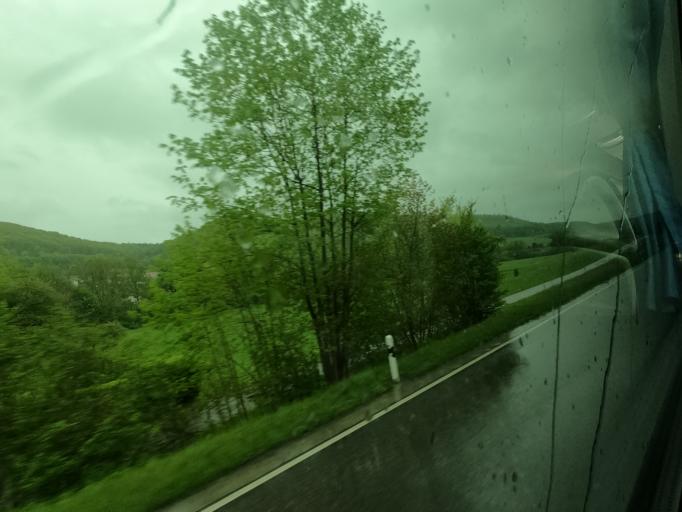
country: DE
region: Baden-Wuerttemberg
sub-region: Regierungsbezirk Stuttgart
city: Oberkochen
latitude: 48.8039
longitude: 10.1252
